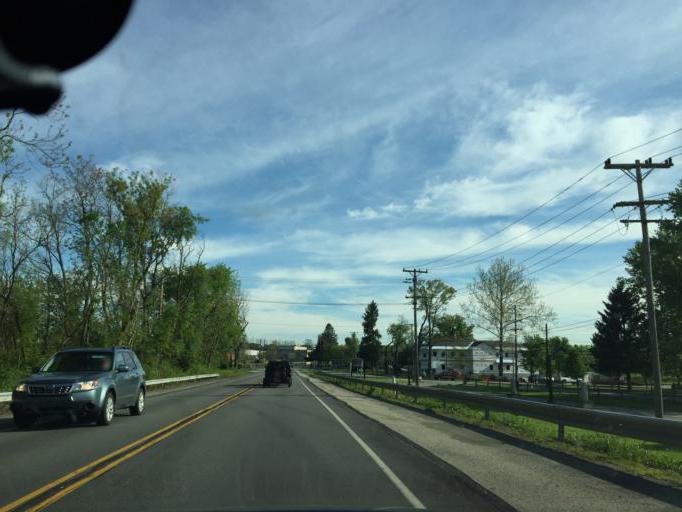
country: US
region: Pennsylvania
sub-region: Westmoreland County
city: Lawson Heights
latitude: 40.3050
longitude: -79.3938
